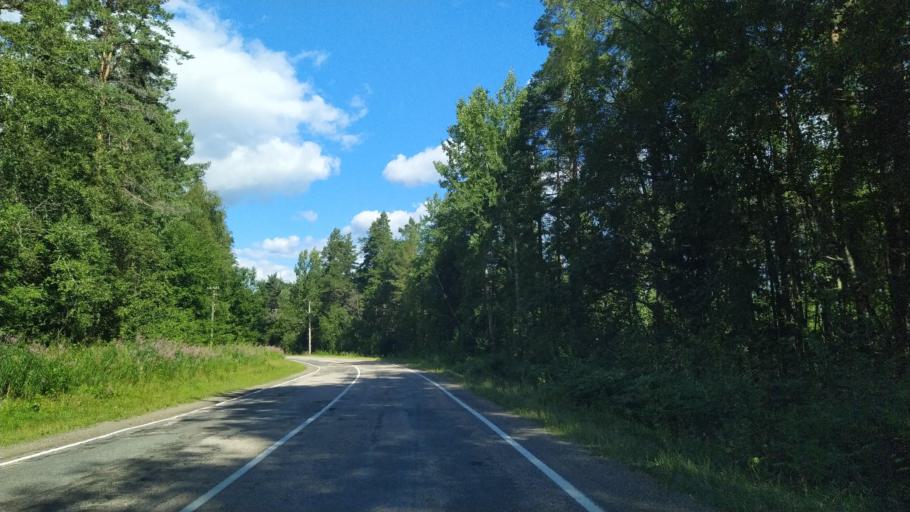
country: RU
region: Leningrad
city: Priozersk
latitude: 60.9729
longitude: 30.2819
